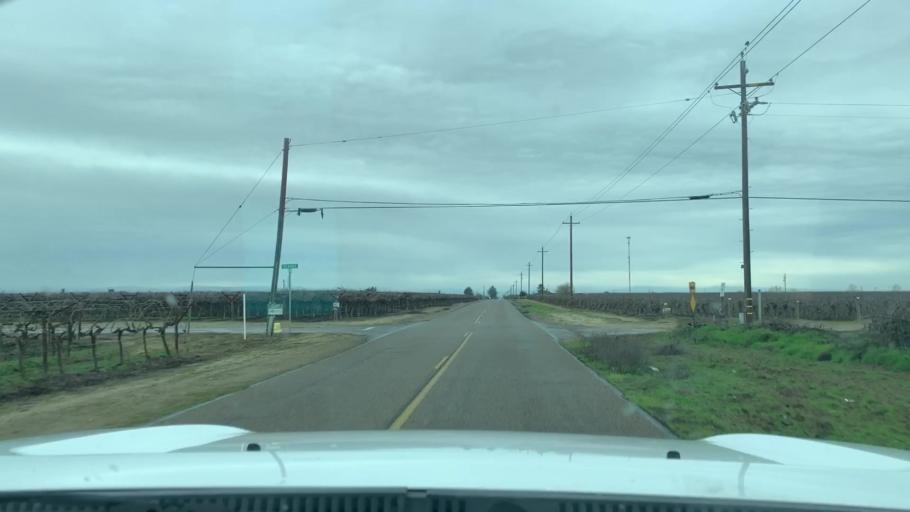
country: US
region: California
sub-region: Fresno County
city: Caruthers
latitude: 36.5474
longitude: -119.7644
